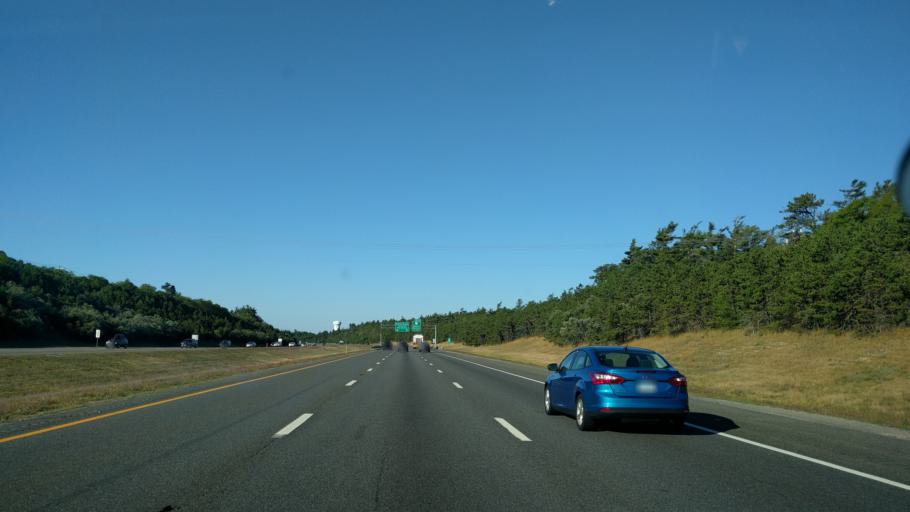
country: US
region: Massachusetts
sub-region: Barnstable County
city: Bourne
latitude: 41.7664
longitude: -70.5892
